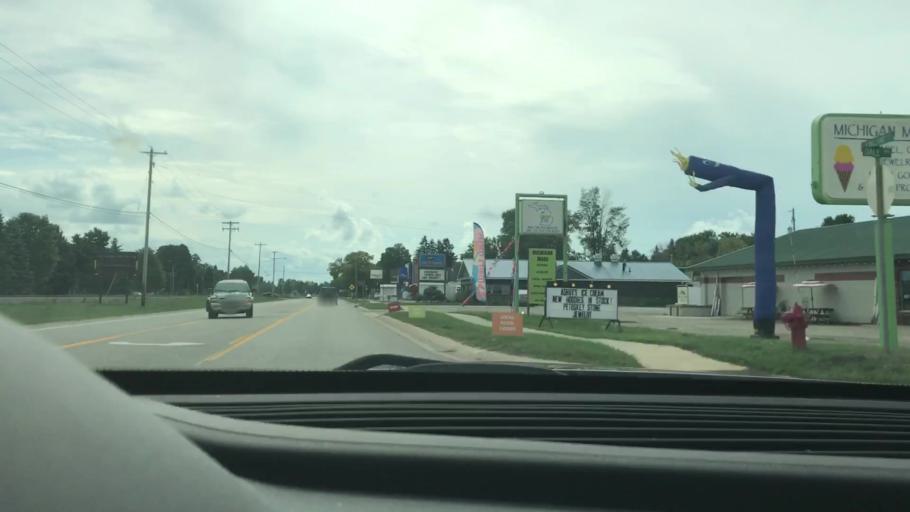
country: US
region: Michigan
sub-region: Antrim County
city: Mancelona
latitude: 44.8972
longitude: -85.0662
